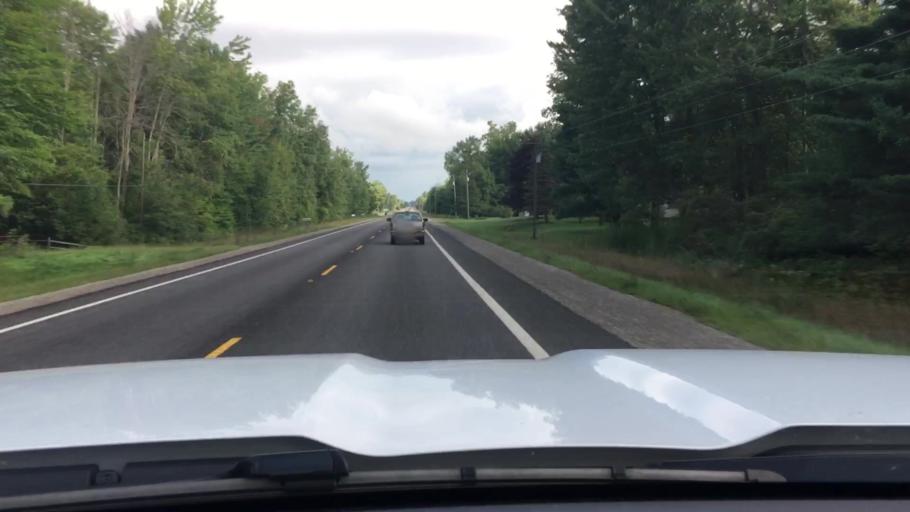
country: US
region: Michigan
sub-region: Tuscola County
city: Caro
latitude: 43.4306
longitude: -83.3848
